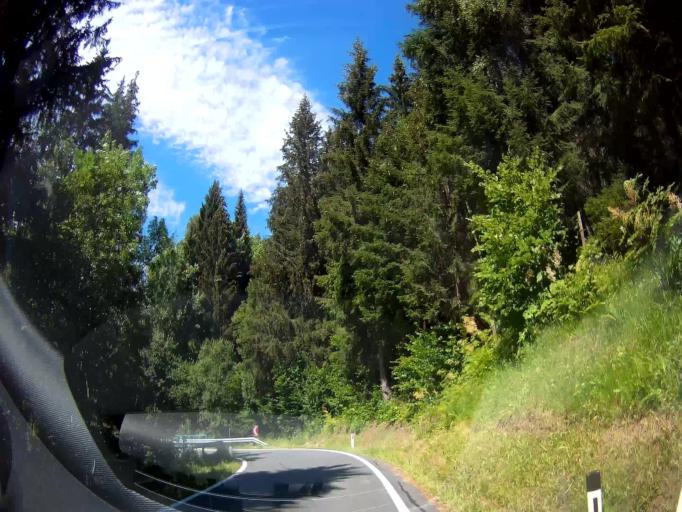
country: AT
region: Carinthia
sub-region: Politischer Bezirk Sankt Veit an der Glan
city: Glodnitz
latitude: 46.9134
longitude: 14.0916
